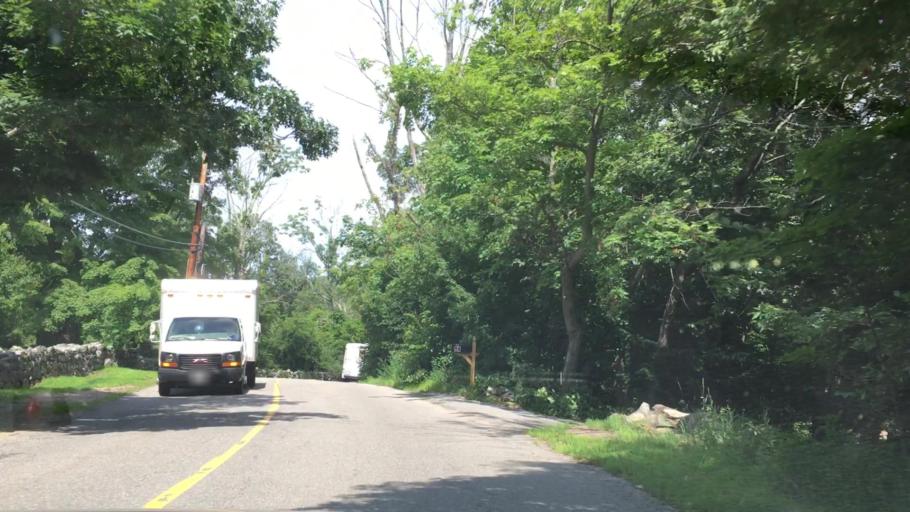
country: US
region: Massachusetts
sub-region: Norfolk County
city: Wellesley
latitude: 42.3324
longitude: -71.2889
